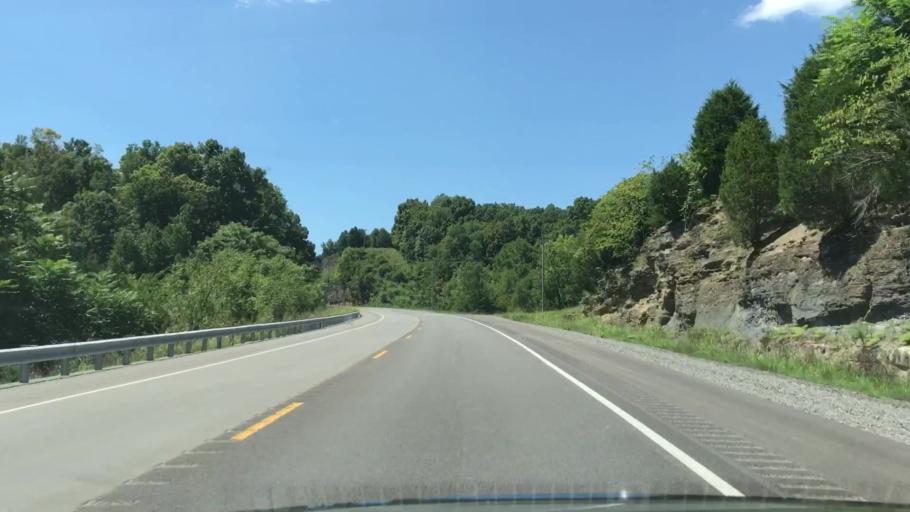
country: US
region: Kentucky
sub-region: Cumberland County
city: Burkesville
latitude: 36.7077
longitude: -85.3687
